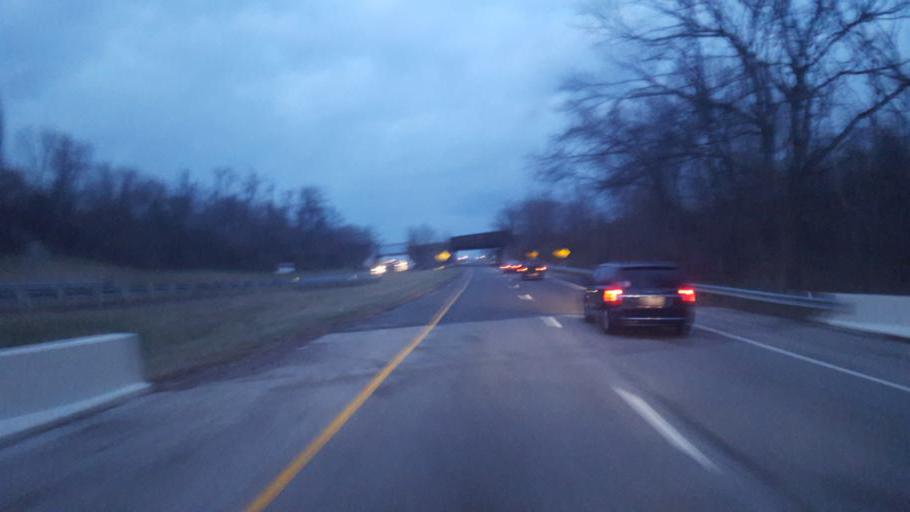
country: US
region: Ohio
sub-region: Ross County
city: Chillicothe
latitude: 39.3794
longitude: -82.9746
